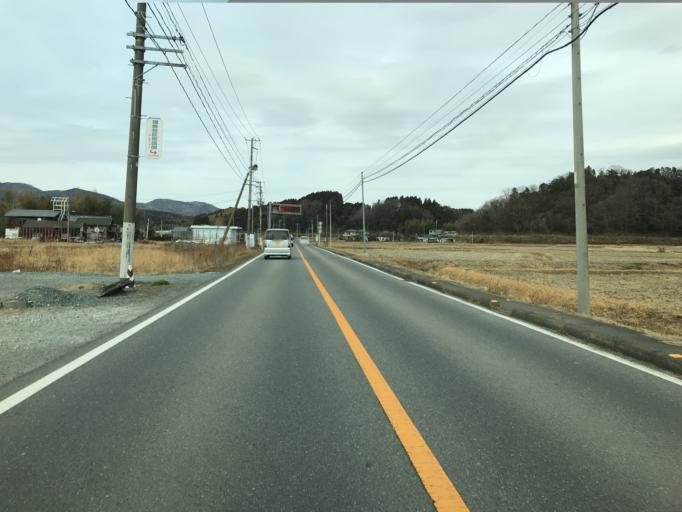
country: JP
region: Fukushima
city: Iwaki
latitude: 37.0890
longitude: 140.8750
